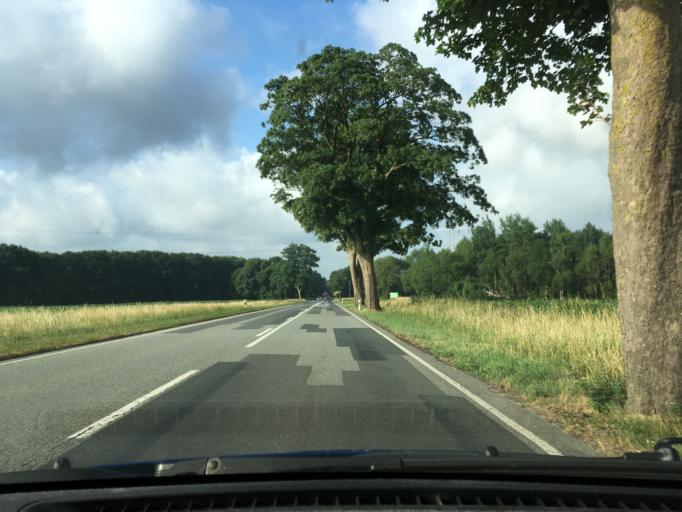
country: DE
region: Lower Saxony
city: Kakenstorf
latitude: 53.3160
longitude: 9.8063
